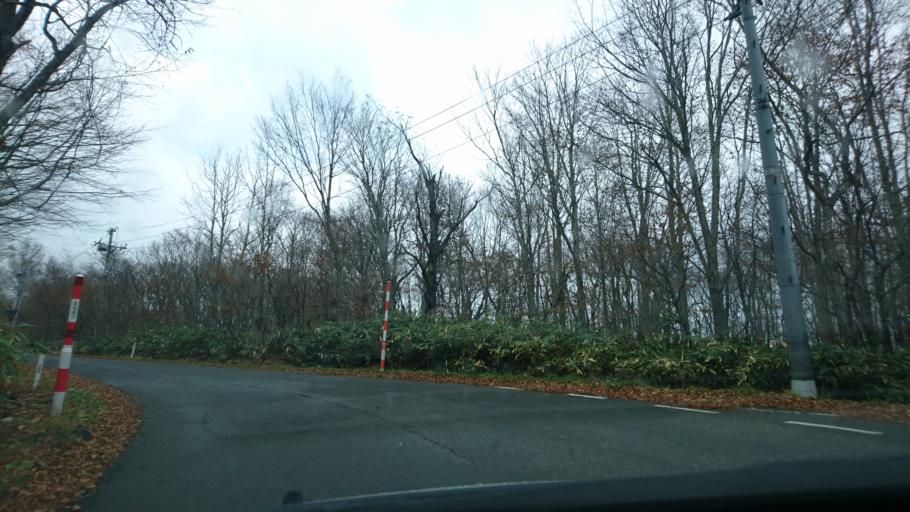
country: JP
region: Iwate
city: Ichinoseki
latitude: 38.9242
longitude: 140.8431
